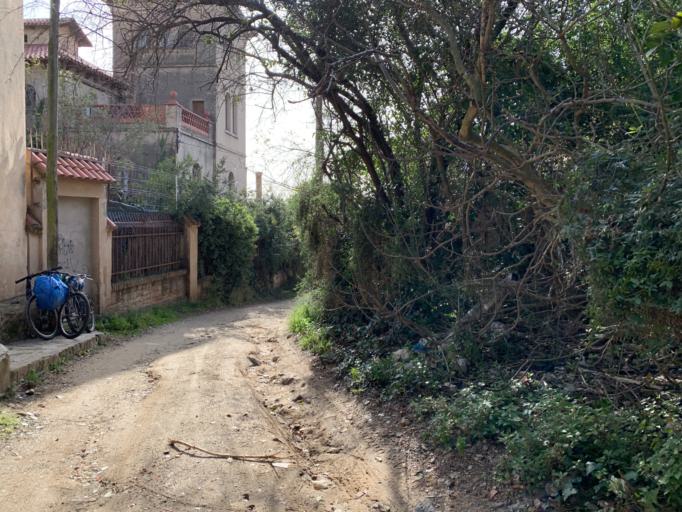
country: ES
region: Catalonia
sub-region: Provincia de Barcelona
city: Montgat
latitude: 41.4730
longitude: 2.2940
